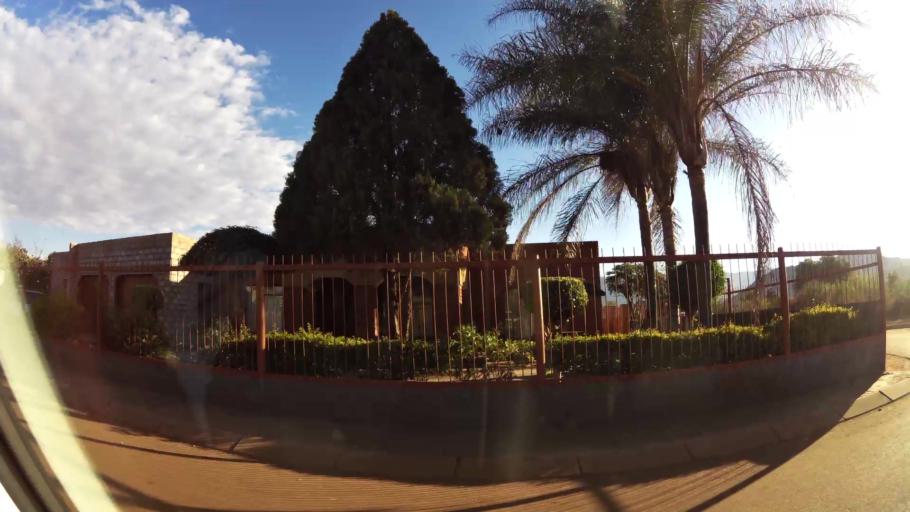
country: ZA
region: Limpopo
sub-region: Waterberg District Municipality
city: Mokopane
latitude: -24.1615
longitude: 28.9877
